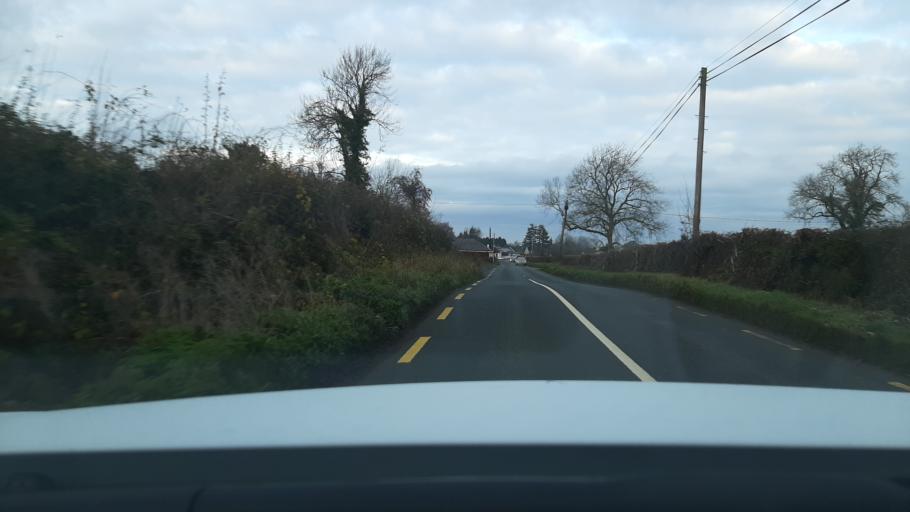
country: IE
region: Leinster
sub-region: Kildare
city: Rathangan
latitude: 53.2320
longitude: -7.0082
